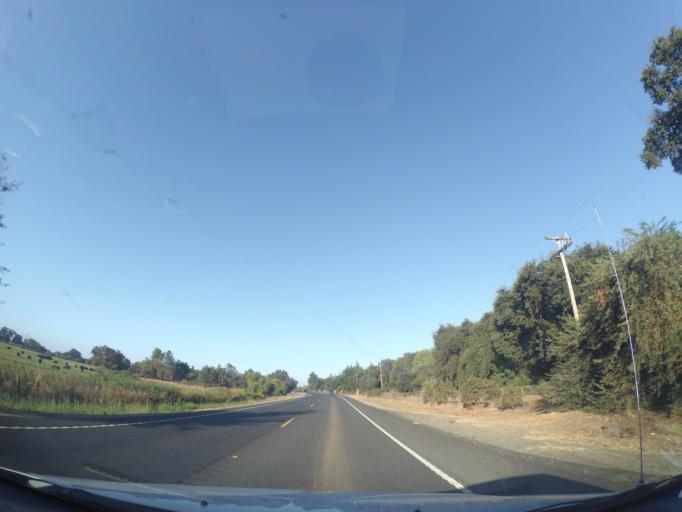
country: US
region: California
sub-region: Merced County
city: Winton
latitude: 37.4980
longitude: -120.4888
